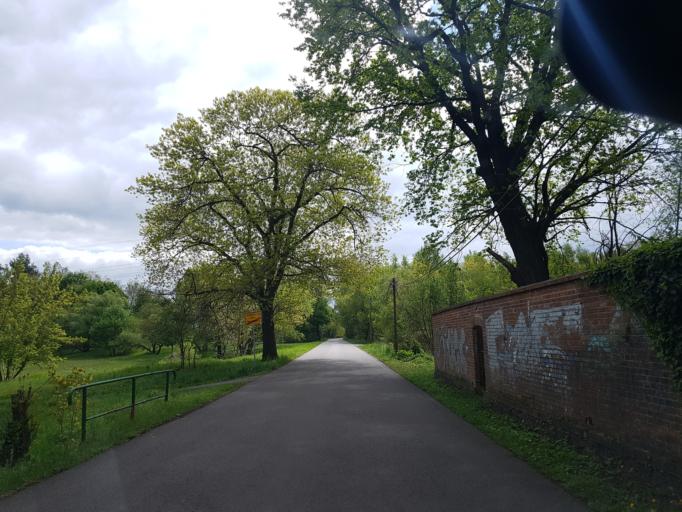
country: DE
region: Brandenburg
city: Altdobern
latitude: 51.6578
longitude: 14.0169
